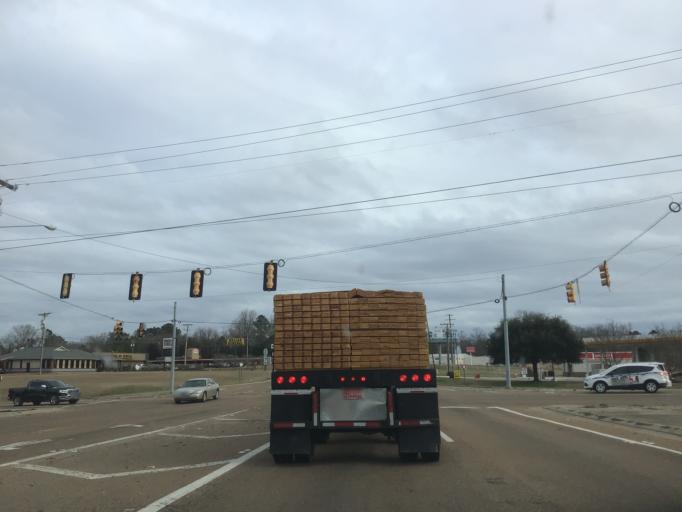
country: US
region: Mississippi
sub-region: Warren County
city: Beechwood
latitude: 32.3447
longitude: -90.8294
